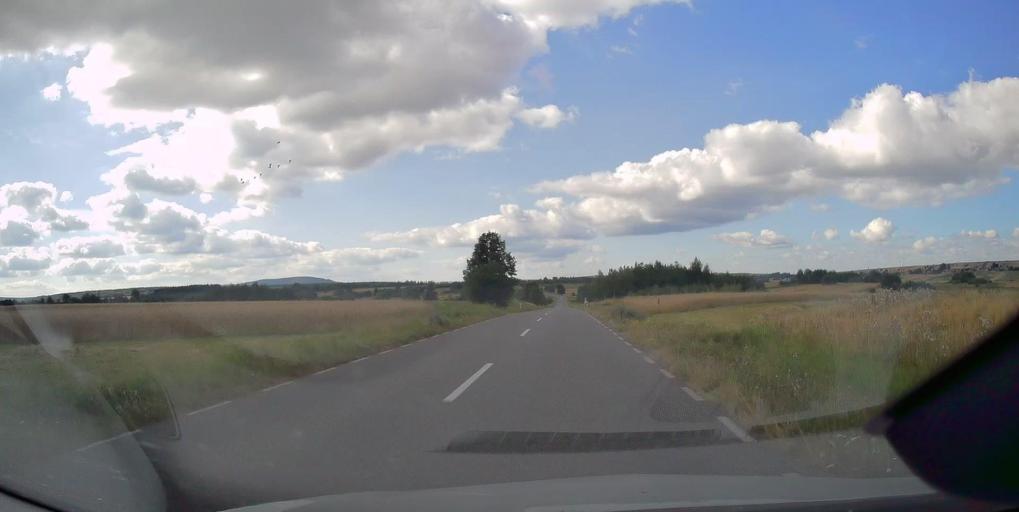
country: PL
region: Swietokrzyskie
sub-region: Powiat kielecki
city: Nowa Slupia
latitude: 50.8960
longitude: 21.0223
